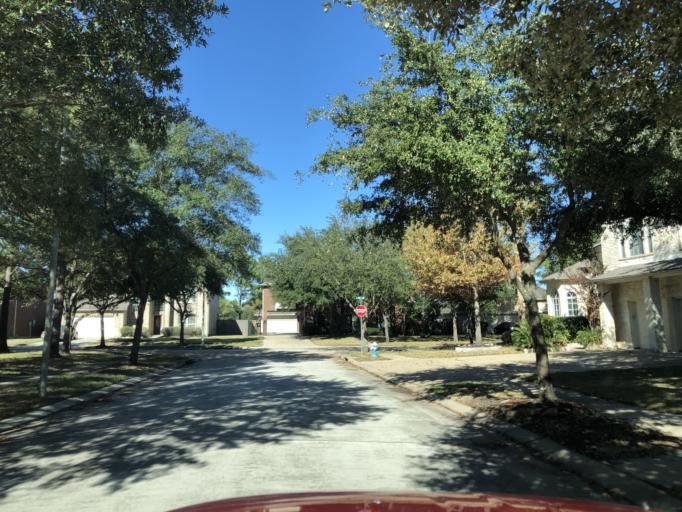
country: US
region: Texas
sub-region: Harris County
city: Cypress
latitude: 29.9414
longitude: -95.6661
